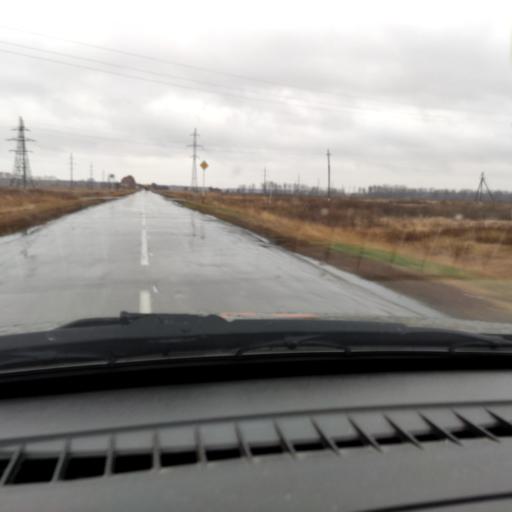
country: RU
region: Samara
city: Khryashchevka
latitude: 53.7327
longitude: 49.1849
